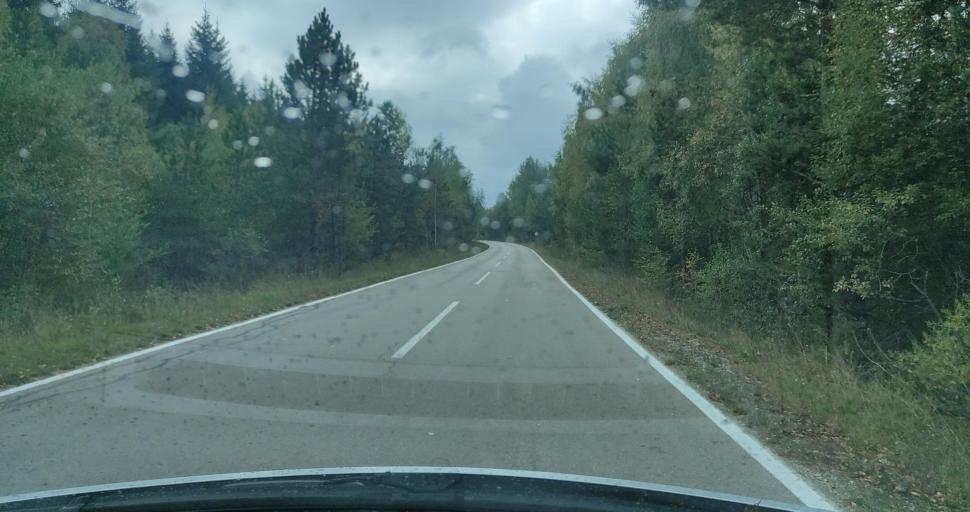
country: RS
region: Central Serbia
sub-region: Jablanicki Okrug
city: Crna Trava
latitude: 42.6857
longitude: 22.3150
